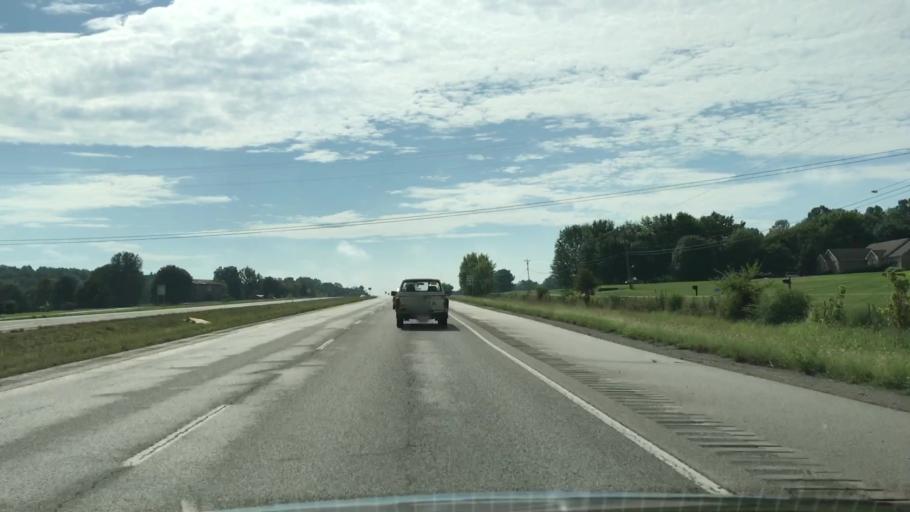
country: US
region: Kentucky
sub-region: Warren County
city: Plano
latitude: 36.8928
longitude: -86.3765
